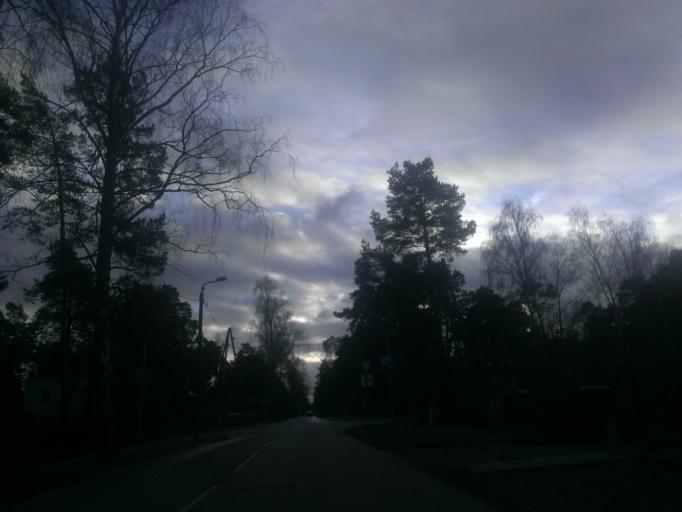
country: LV
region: Riga
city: Bolderaja
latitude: 57.0714
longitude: 24.1048
